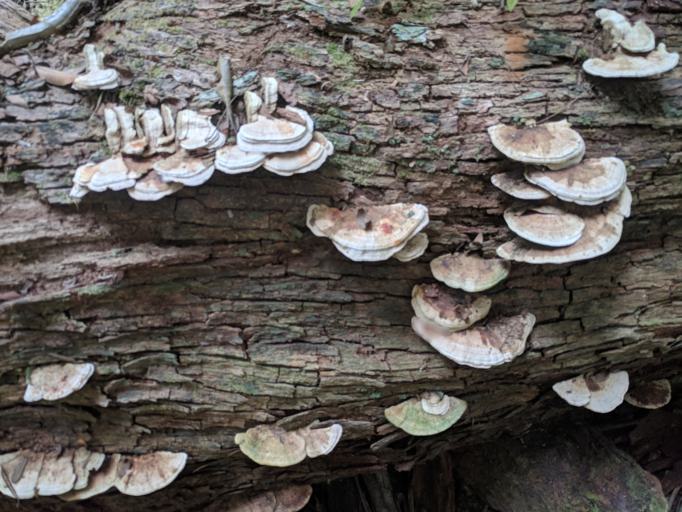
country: AU
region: Queensland
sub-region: Tablelands
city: Kuranda
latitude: -16.8186
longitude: 145.6350
